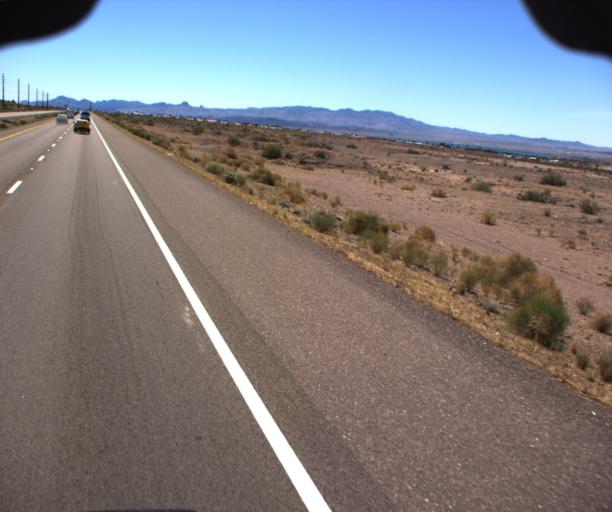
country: US
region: Arizona
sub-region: Mohave County
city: Desert Hills
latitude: 34.5598
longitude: -114.3601
